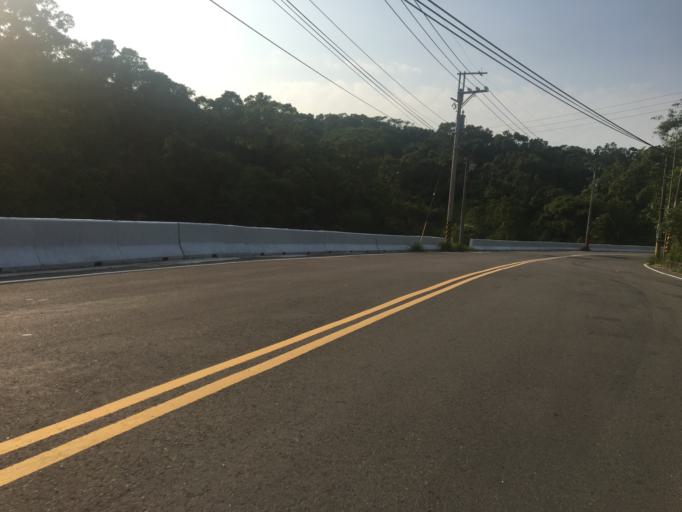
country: TW
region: Taiwan
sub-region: Hsinchu
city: Hsinchu
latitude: 24.7659
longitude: 120.9478
